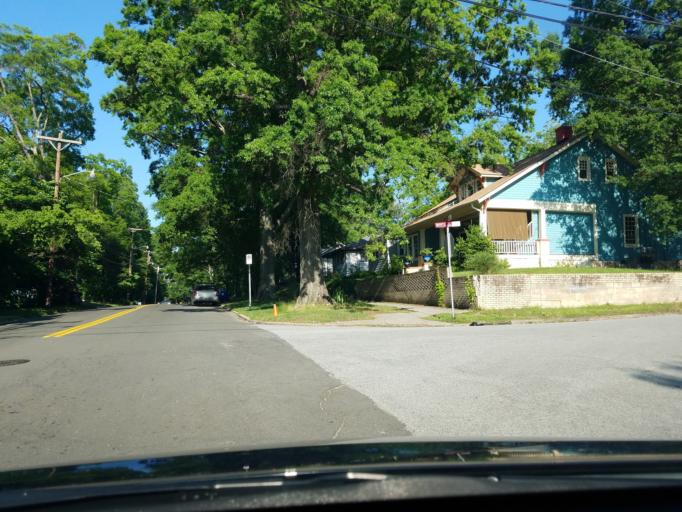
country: US
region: North Carolina
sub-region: Durham County
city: Durham
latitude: 36.0055
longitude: -78.8982
